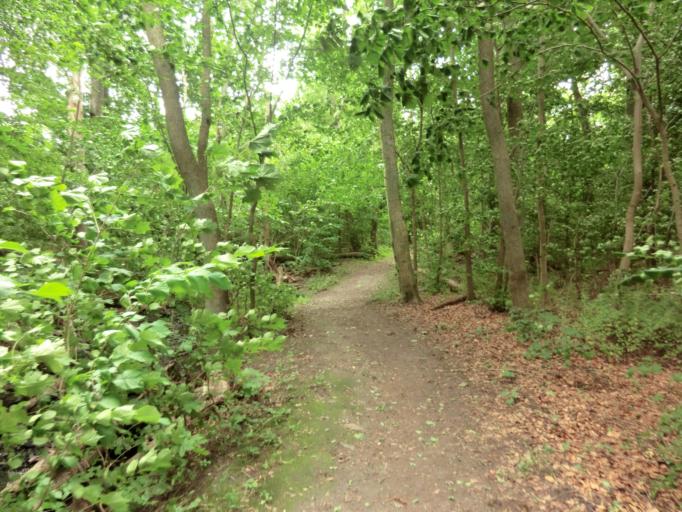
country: SE
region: Skane
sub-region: Lunds Kommun
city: Genarp
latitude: 55.7136
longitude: 13.3271
